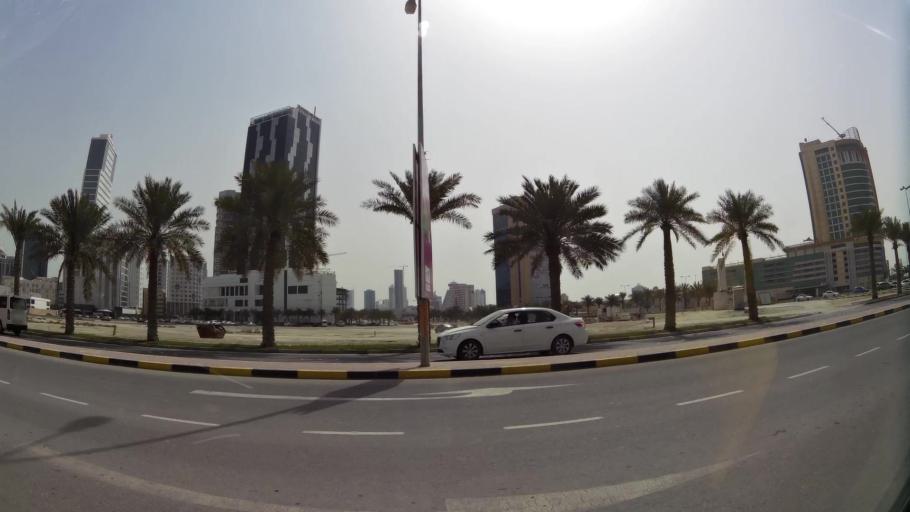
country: BH
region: Manama
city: Jidd Hafs
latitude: 26.2356
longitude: 50.5341
